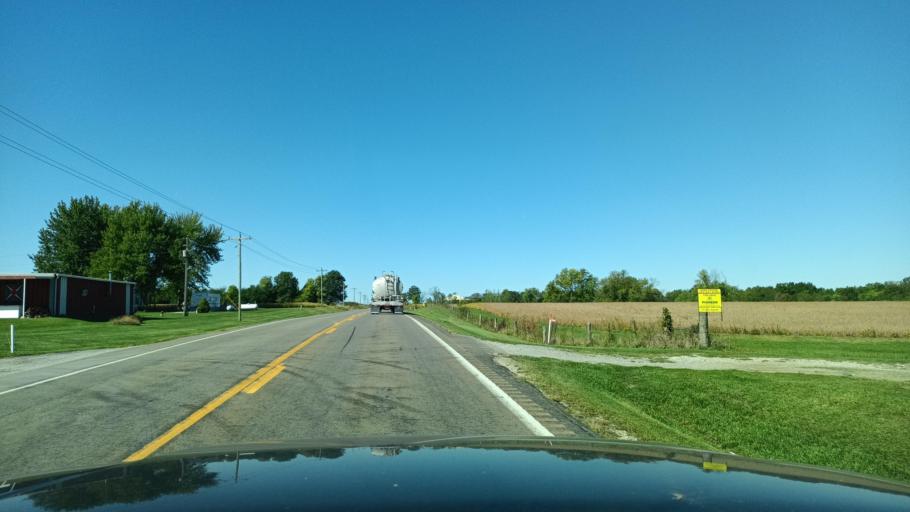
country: US
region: Missouri
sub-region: Scotland County
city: Memphis
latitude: 40.4546
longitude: -92.0324
